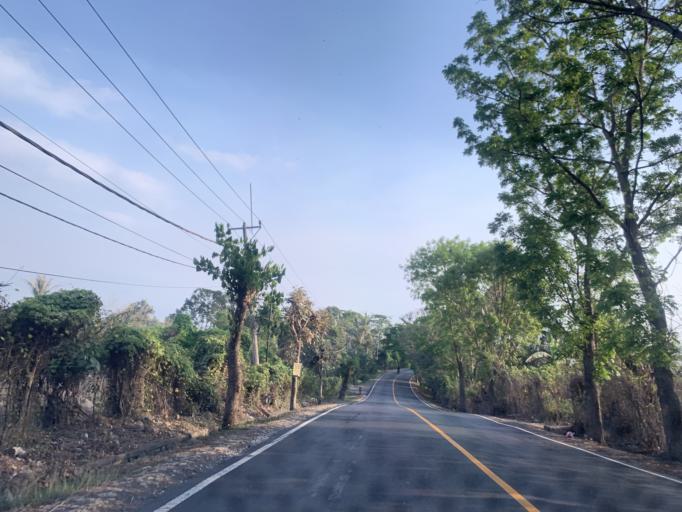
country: ID
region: Bali
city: Banjar Delodrurung
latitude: -8.5089
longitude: 115.0174
